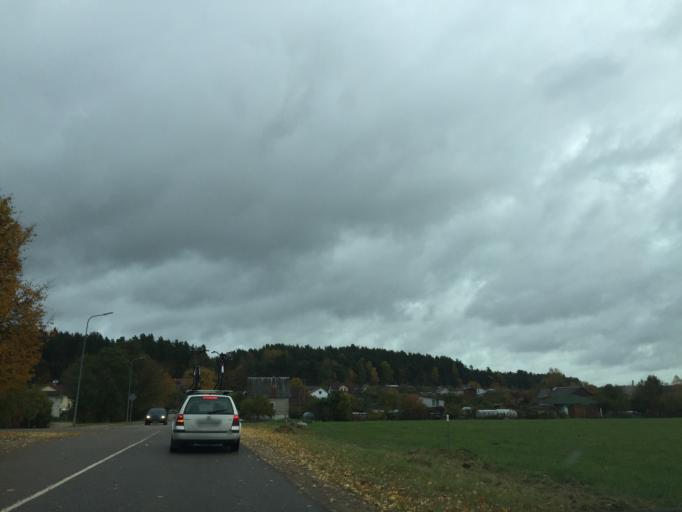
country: LV
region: Ogre
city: Ogre
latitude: 56.7951
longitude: 24.6336
